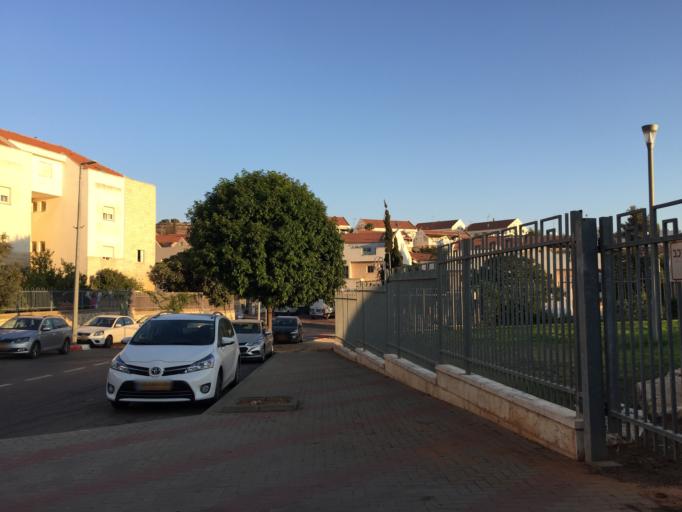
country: PS
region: West Bank
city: Marda
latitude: 32.1039
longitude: 35.1954
